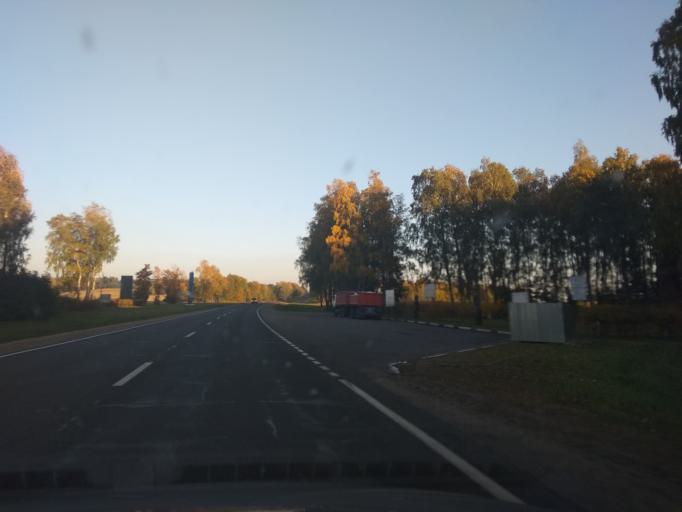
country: BY
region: Grodnenskaya
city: Vawkavysk
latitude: 53.1452
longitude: 24.6096
